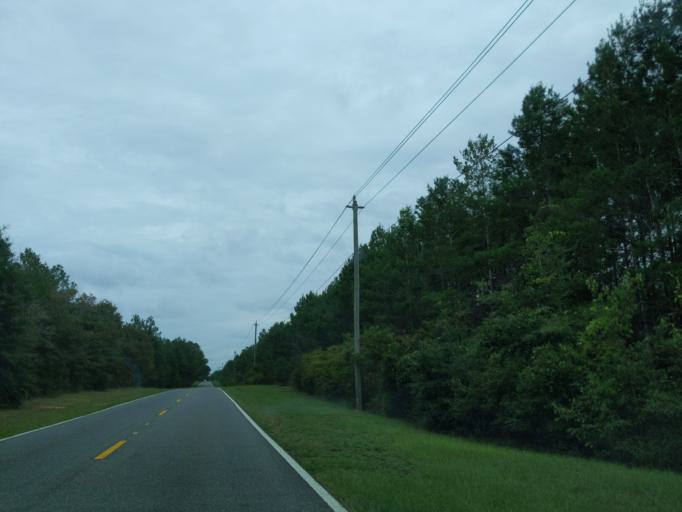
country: US
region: Florida
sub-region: Leon County
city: Woodville
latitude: 30.3707
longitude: -84.1901
